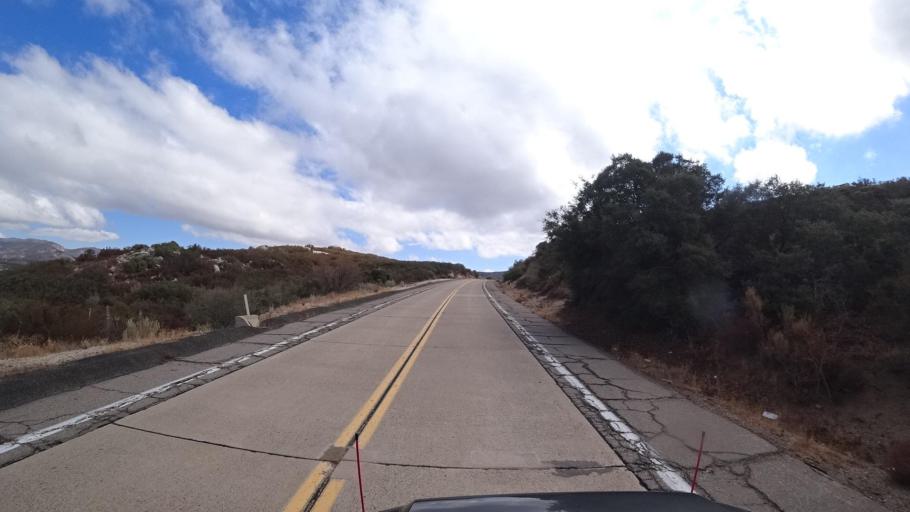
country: US
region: California
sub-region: San Diego County
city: Campo
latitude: 32.7195
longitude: -116.4006
